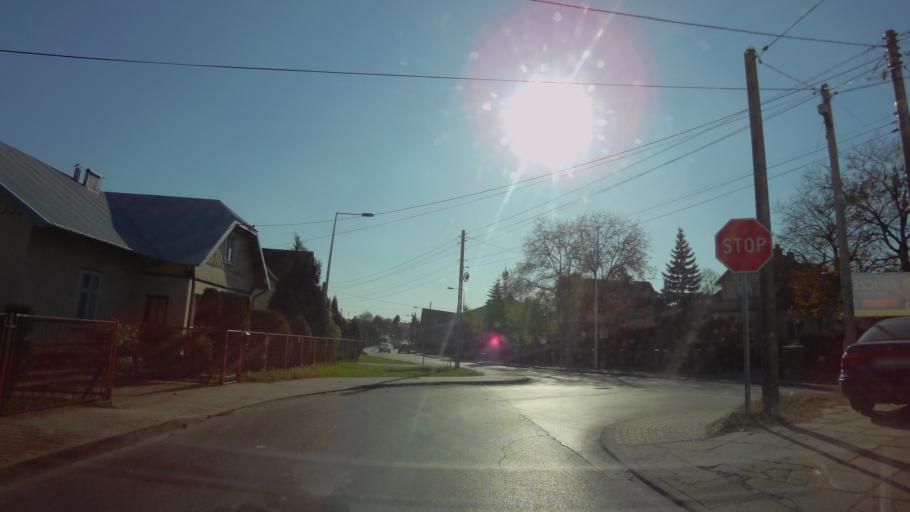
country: PL
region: Subcarpathian Voivodeship
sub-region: Powiat lezajski
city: Lezajsk
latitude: 50.2625
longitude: 22.4240
